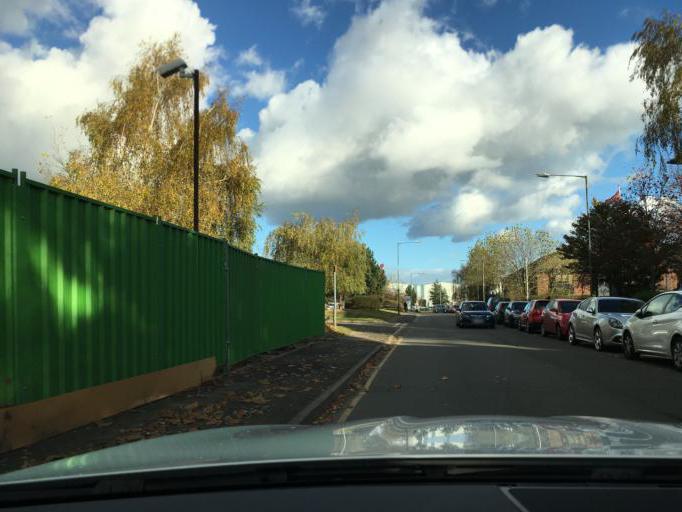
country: GB
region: England
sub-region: Warwickshire
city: Royal Leamington Spa
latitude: 52.2768
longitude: -1.5486
